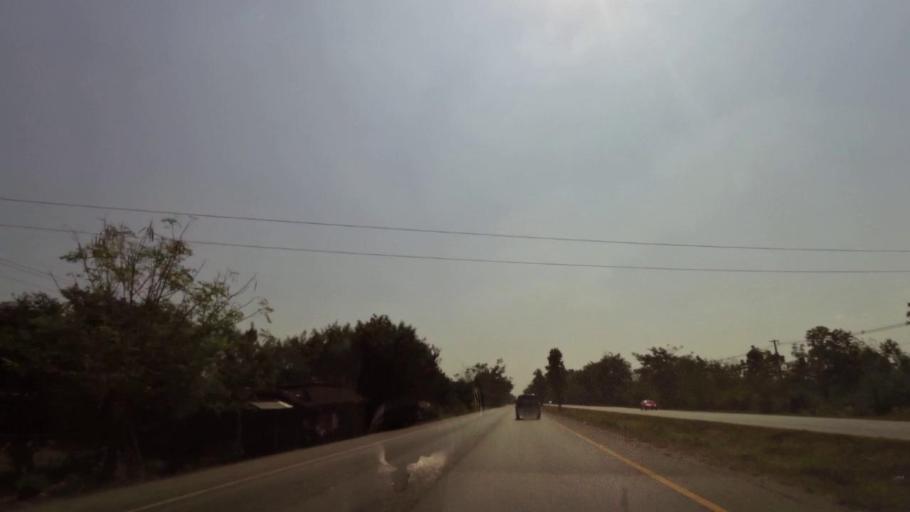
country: TH
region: Phichit
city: Bueng Na Rang
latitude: 16.3325
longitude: 100.1284
